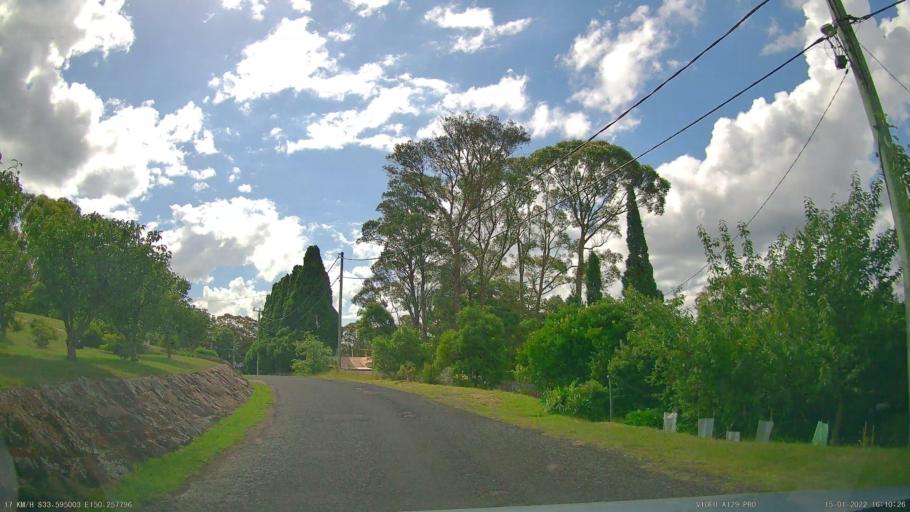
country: AU
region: New South Wales
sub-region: Blue Mountains Municipality
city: Blackheath
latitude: -33.5950
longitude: 150.2577
